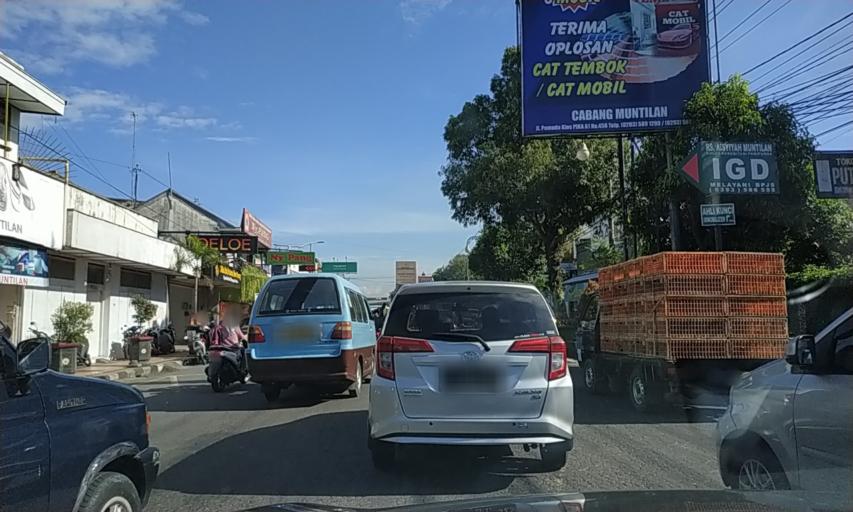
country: ID
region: Central Java
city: Muntilan
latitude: -7.5847
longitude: 110.2872
